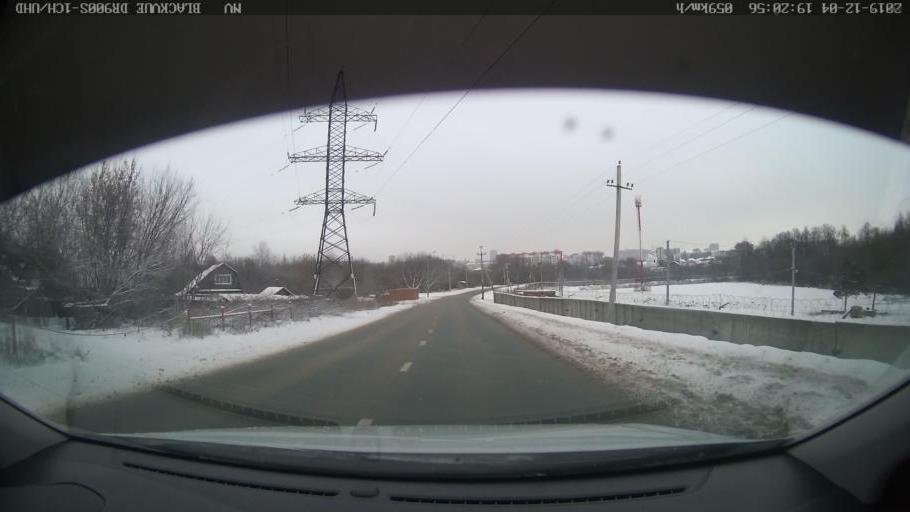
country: RU
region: Tatarstan
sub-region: Gorod Kazan'
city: Kazan
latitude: 55.8145
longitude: 49.2122
